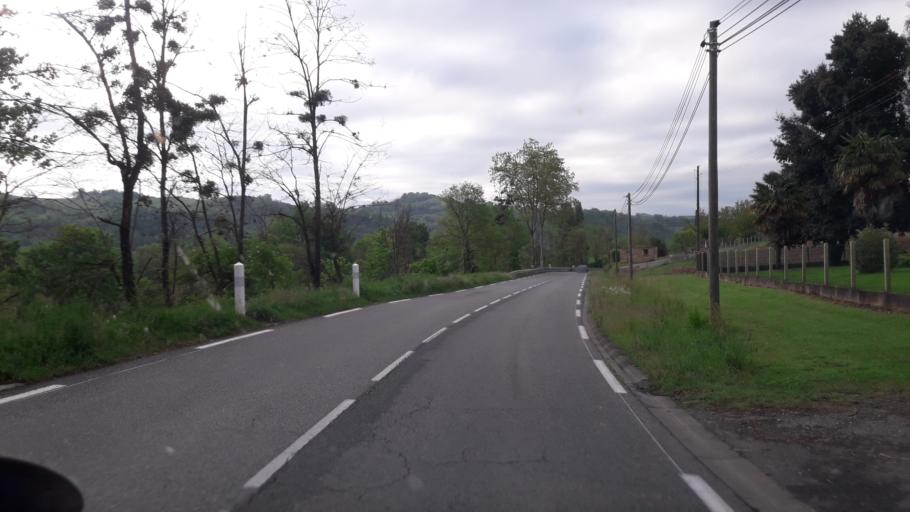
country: FR
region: Midi-Pyrenees
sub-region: Departement de la Haute-Garonne
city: Cazeres
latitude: 43.1984
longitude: 1.1017
